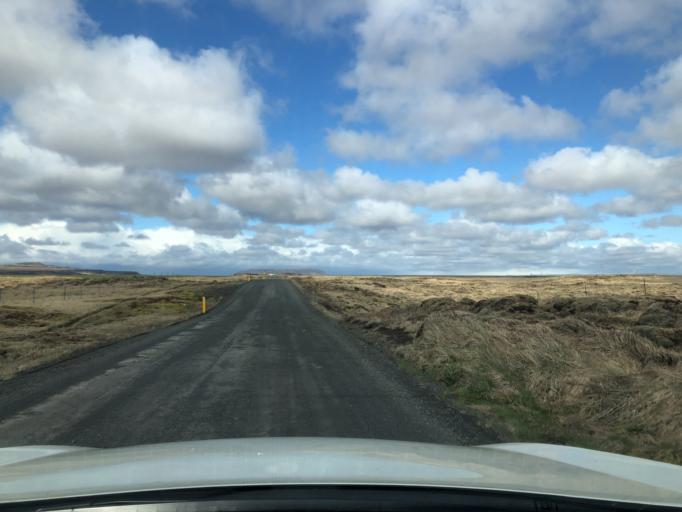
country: IS
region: South
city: Selfoss
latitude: 63.9285
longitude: -20.6722
